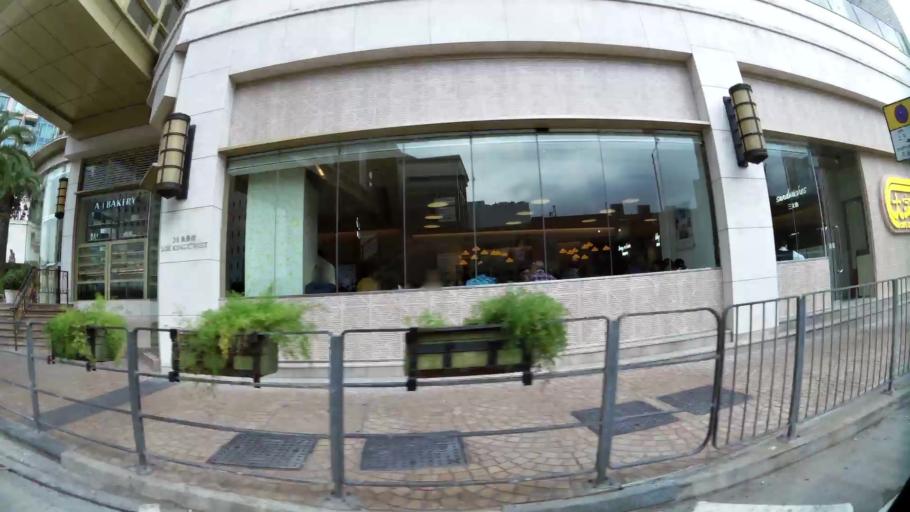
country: HK
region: Sha Tin
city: Sha Tin
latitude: 22.3952
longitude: 114.1986
